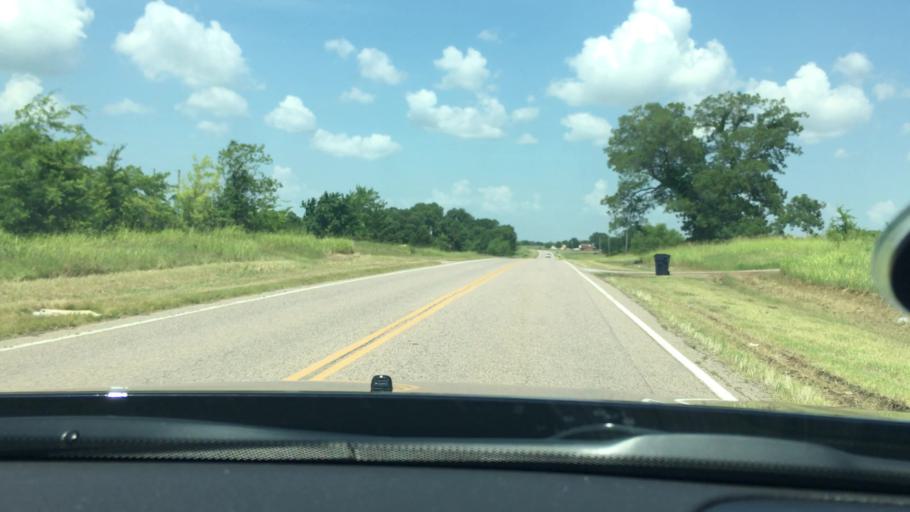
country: US
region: Oklahoma
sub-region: Bryan County
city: Durant
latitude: 34.0857
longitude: -96.3940
